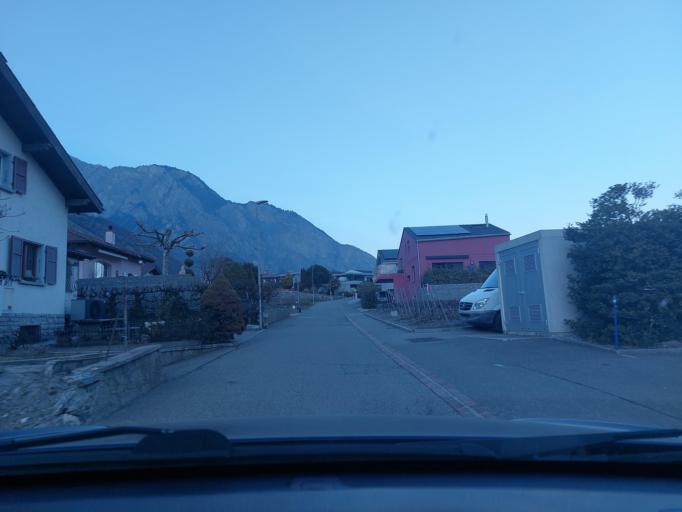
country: CH
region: Valais
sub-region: Martigny District
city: Leytron
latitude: 46.1867
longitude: 7.2127
